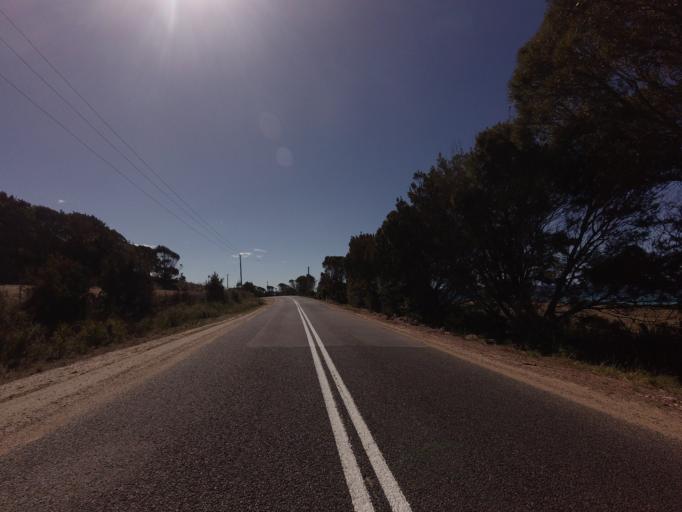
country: AU
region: Tasmania
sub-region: Break O'Day
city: St Helens
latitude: -41.7961
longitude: 148.2618
